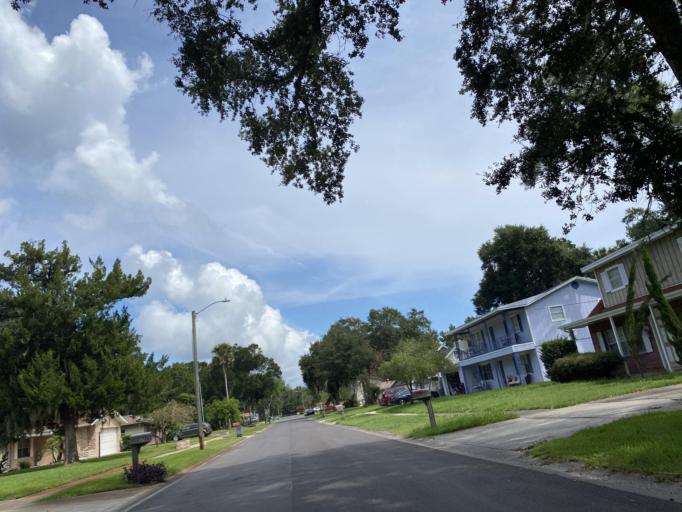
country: US
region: Florida
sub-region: Volusia County
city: Port Orange
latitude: 29.1330
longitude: -81.0049
